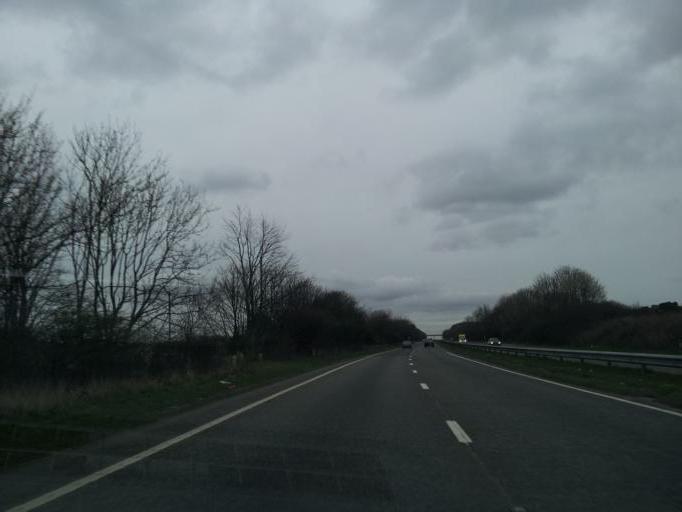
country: GB
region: England
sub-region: Cornwall
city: Redruth
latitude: 50.2492
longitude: -5.2232
